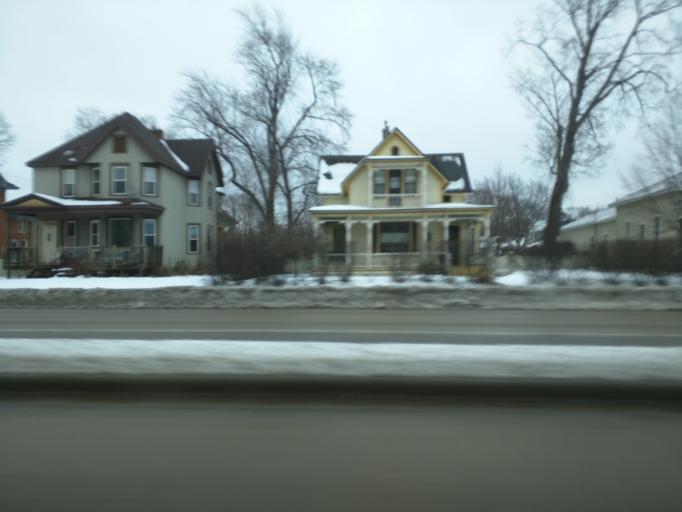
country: US
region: Wisconsin
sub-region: La Crosse County
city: La Crosse
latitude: 43.8042
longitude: -91.2395
